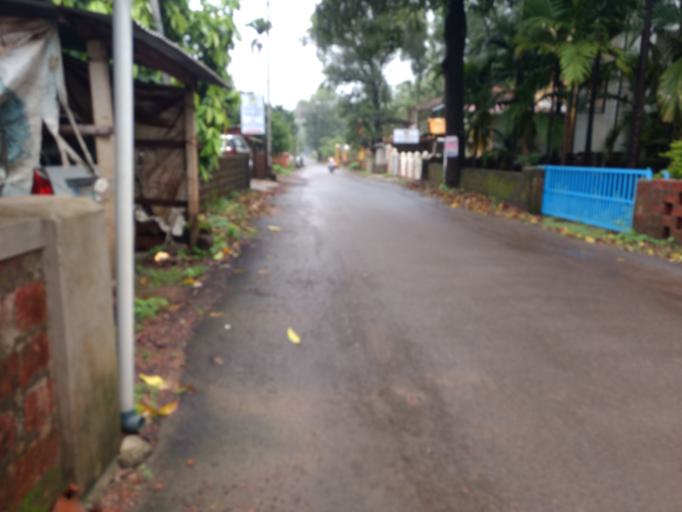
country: IN
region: Maharashtra
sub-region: Ratnagiri
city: Guhagar
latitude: 17.4941
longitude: 73.1866
